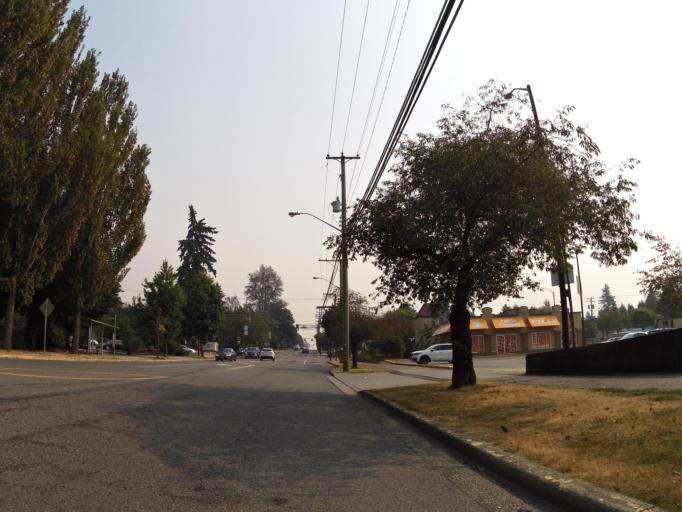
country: CA
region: British Columbia
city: Delta
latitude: 49.1560
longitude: -122.9136
